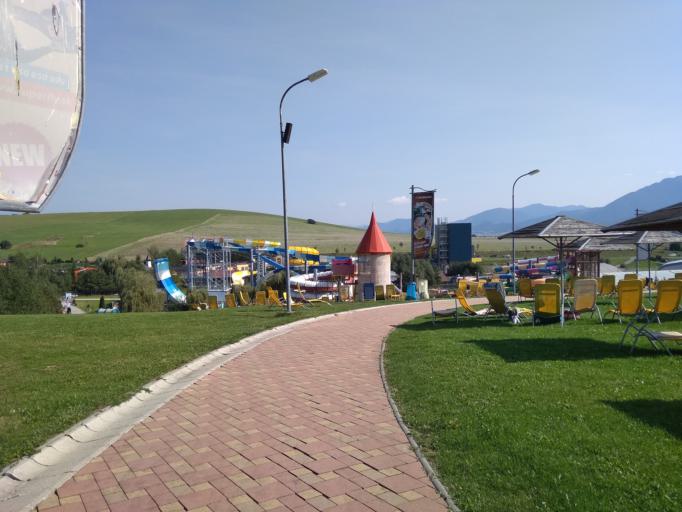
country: SK
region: Zilinsky
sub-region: Okres Liptovsky Mikulas
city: Liptovsky Mikulas
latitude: 49.1077
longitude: 19.5705
